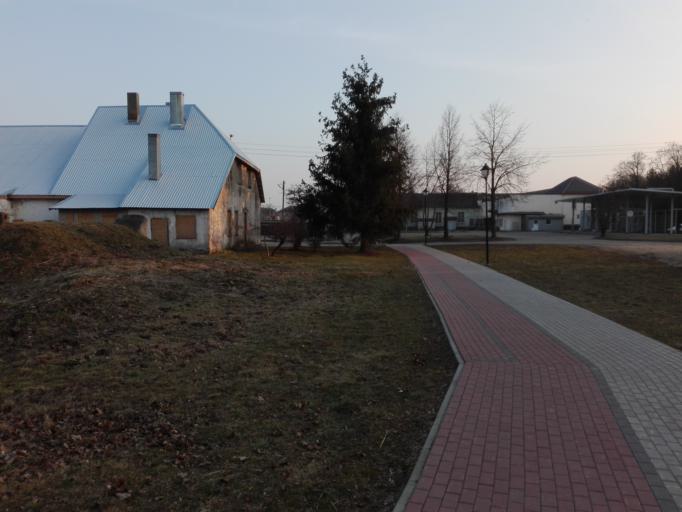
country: LT
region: Panevezys
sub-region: Birzai
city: Birzai
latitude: 56.2070
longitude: 24.7607
